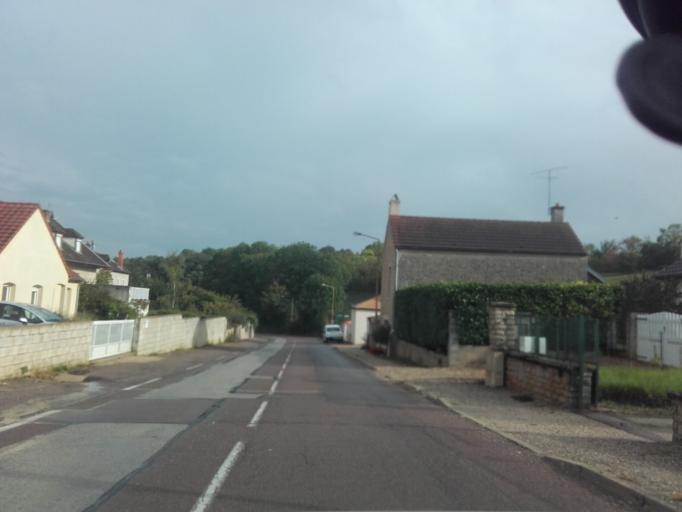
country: FR
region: Bourgogne
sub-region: Departement de la Cote-d'Or
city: Savigny-les-Beaune
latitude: 47.0497
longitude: 4.7736
